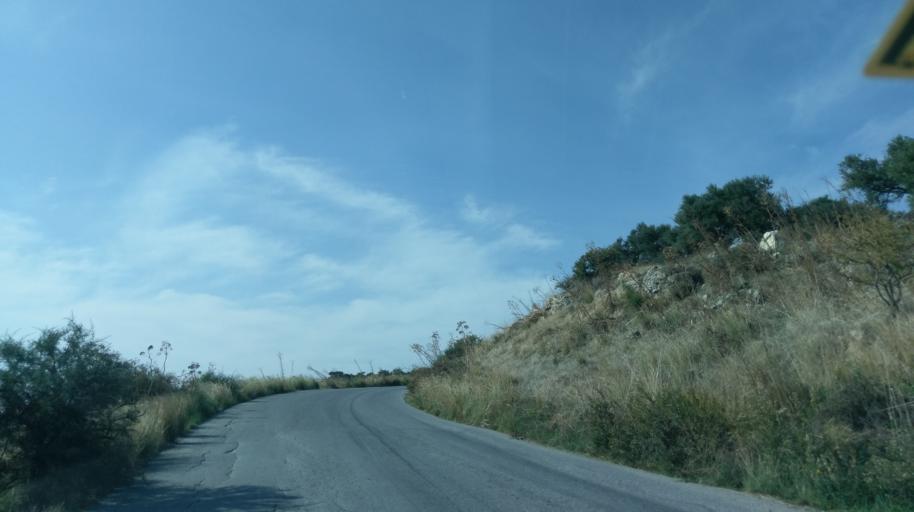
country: CY
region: Keryneia
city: Lapithos
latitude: 35.2993
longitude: 33.1778
